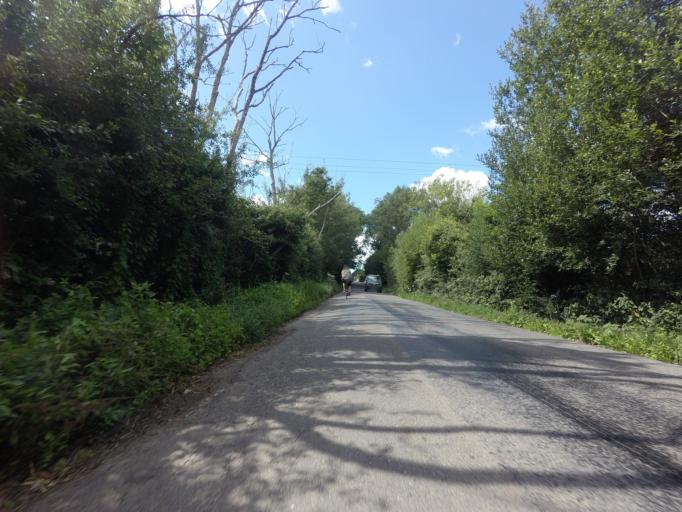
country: GB
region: England
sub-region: East Sussex
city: Horam
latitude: 50.8927
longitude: 0.1857
